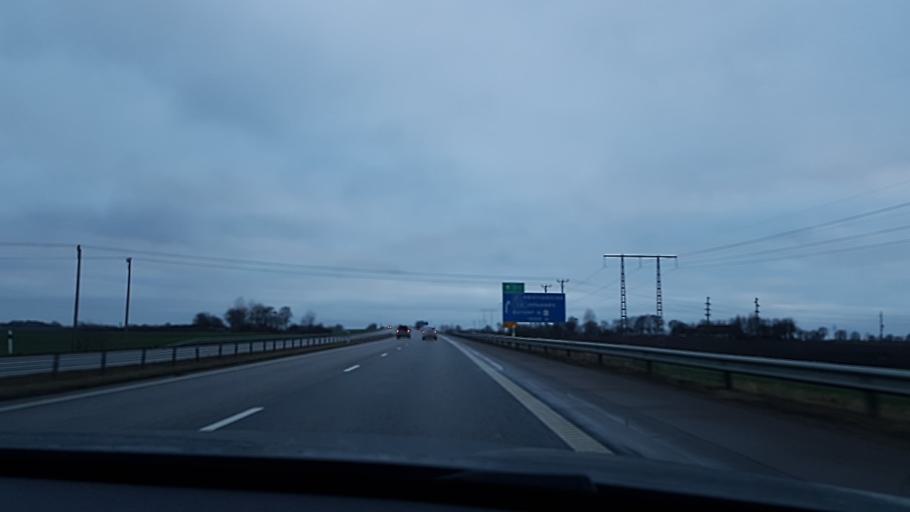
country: SE
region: Skane
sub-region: Astorps Kommun
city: Astorp
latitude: 56.1556
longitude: 12.9523
